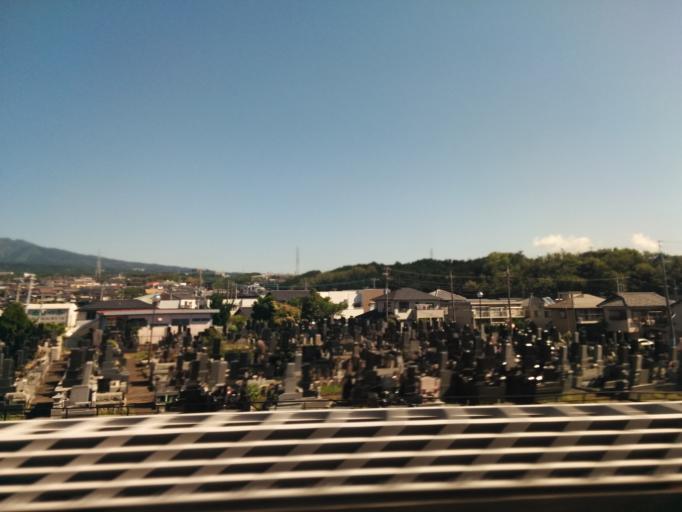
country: JP
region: Shizuoka
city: Numazu
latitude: 35.1245
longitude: 138.8630
